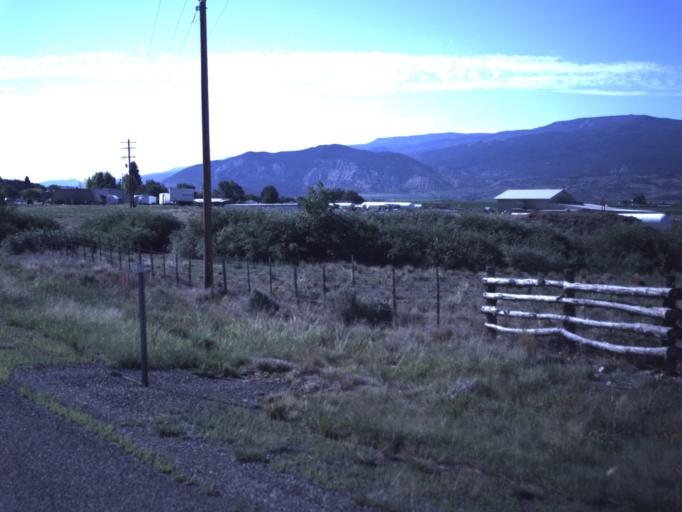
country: US
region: Utah
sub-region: Wayne County
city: Loa
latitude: 38.3445
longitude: -111.5557
